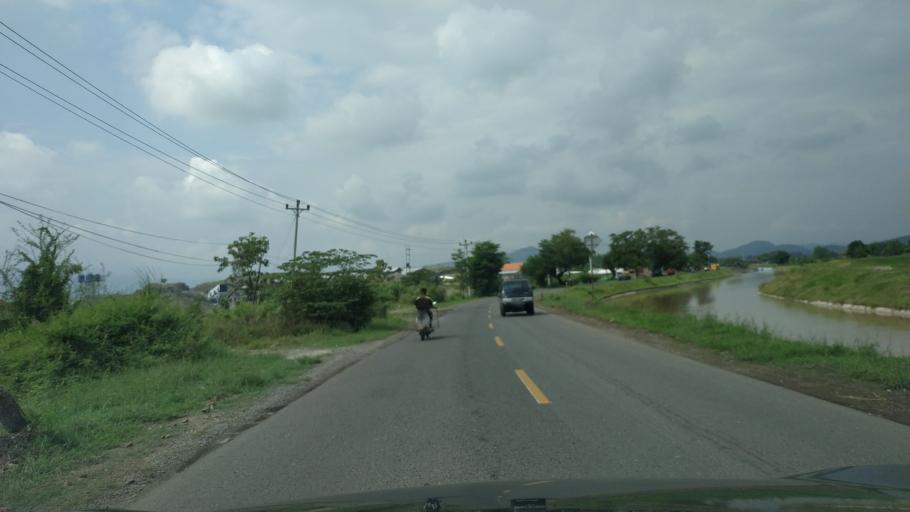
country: ID
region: Central Java
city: Margasari
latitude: -7.0851
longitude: 108.9840
